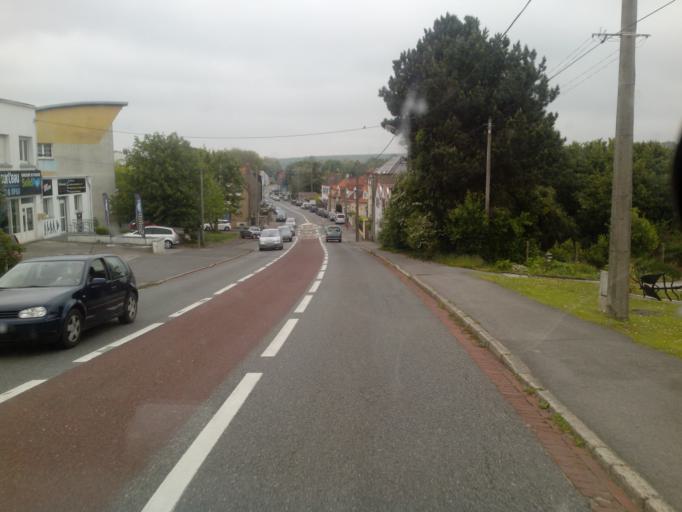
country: FR
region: Nord-Pas-de-Calais
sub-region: Departement du Pas-de-Calais
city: Saint-Etienne-au-Mont
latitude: 50.6749
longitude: 1.6366
